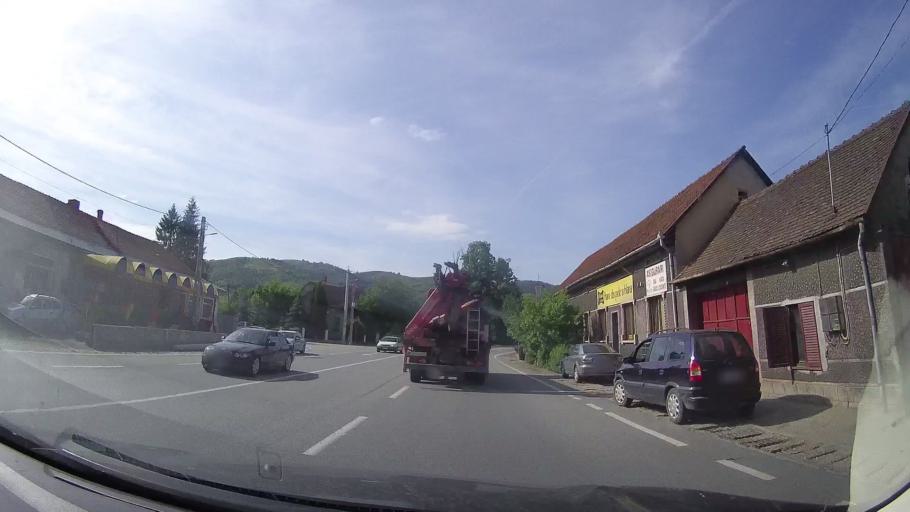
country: RO
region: Caras-Severin
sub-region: Comuna Teregova
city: Teregova
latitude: 45.1557
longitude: 22.3029
